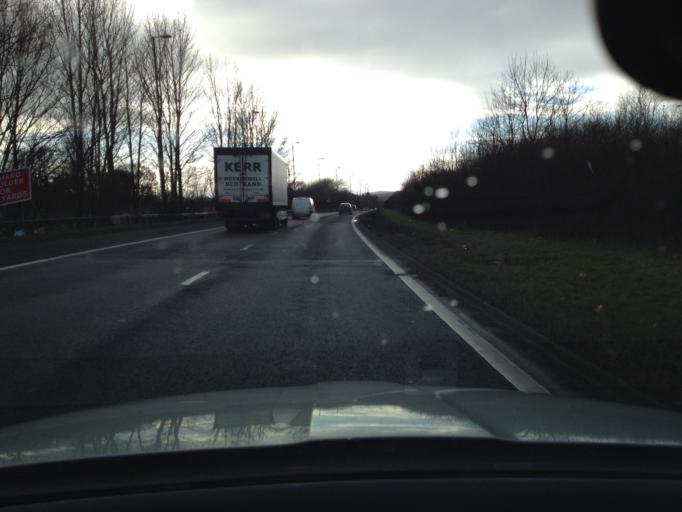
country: GB
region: Scotland
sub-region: Edinburgh
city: Newbridge
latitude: 55.9251
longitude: -3.4106
